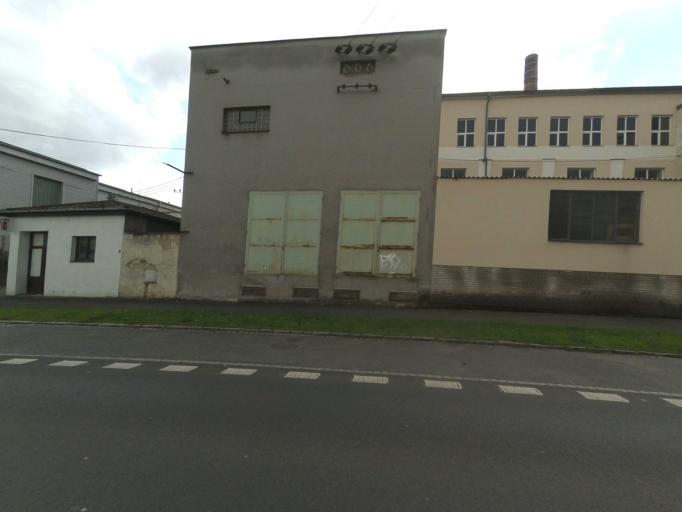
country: CZ
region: Plzensky
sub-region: Okres Domazlice
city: Domazlice
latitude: 49.4338
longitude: 12.9518
